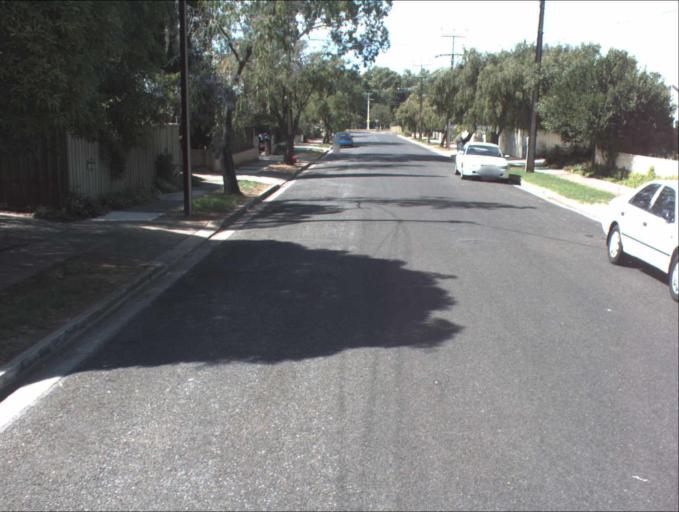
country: AU
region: South Australia
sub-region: Port Adelaide Enfield
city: Klemzig
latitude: -34.8798
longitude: 138.6467
